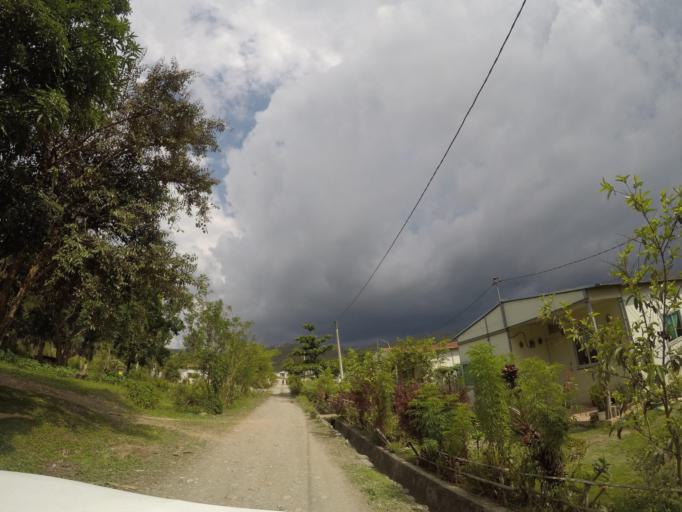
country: TL
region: Ermera
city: Gleno
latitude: -8.7101
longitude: 125.4531
